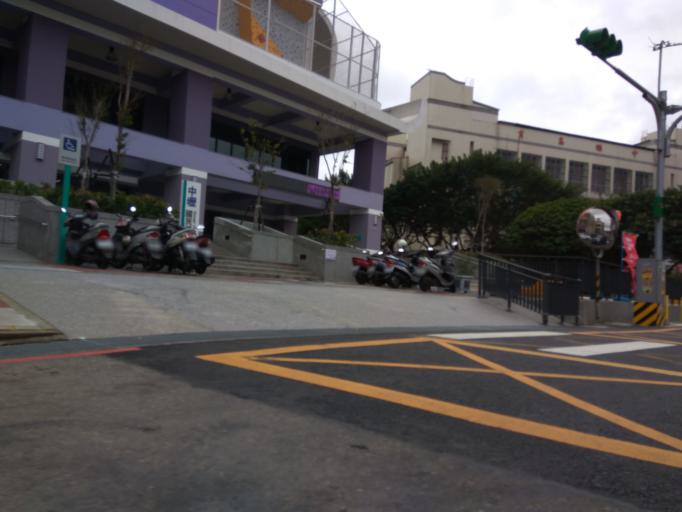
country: TW
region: Taiwan
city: Taoyuan City
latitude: 24.9641
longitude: 121.2155
